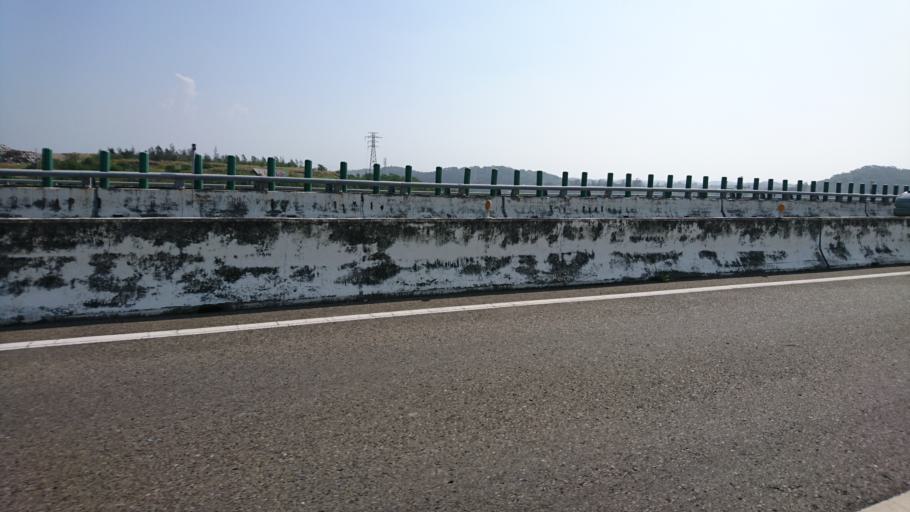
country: TW
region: Taiwan
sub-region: Miaoli
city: Miaoli
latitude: 24.6715
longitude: 120.8368
